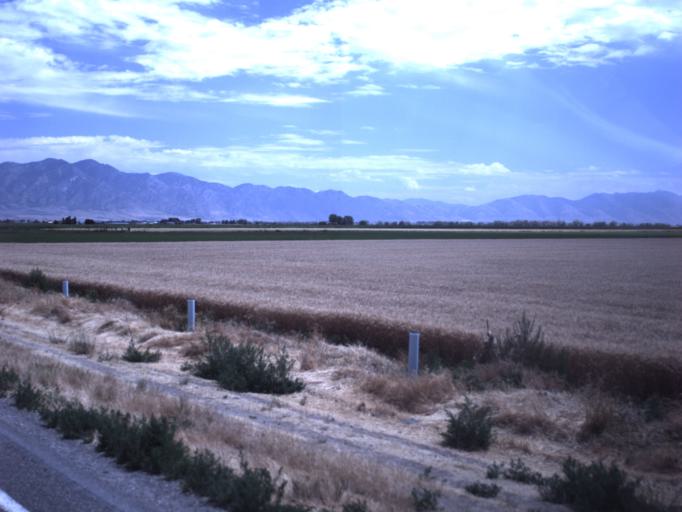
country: US
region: Utah
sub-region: Box Elder County
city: Tremonton
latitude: 41.7095
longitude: -112.2714
